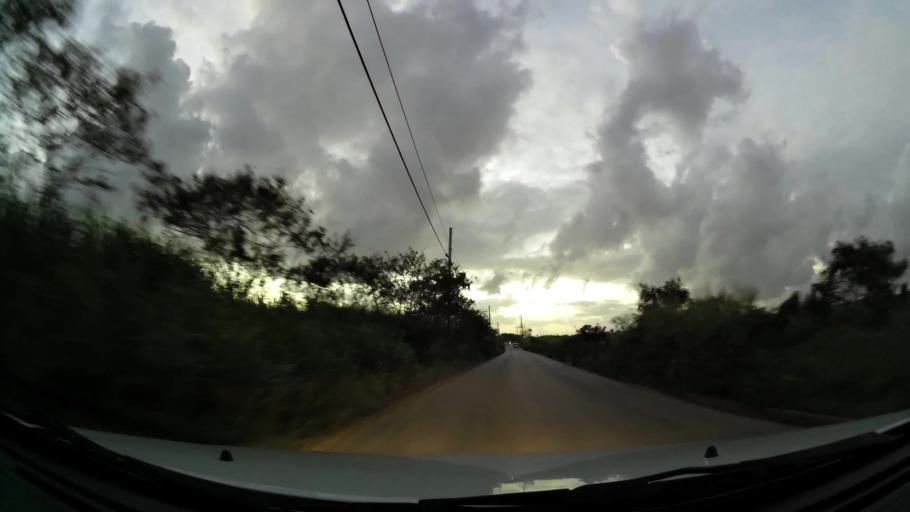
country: BB
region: Saint Philip
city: Crane
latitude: 13.1181
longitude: -59.4891
